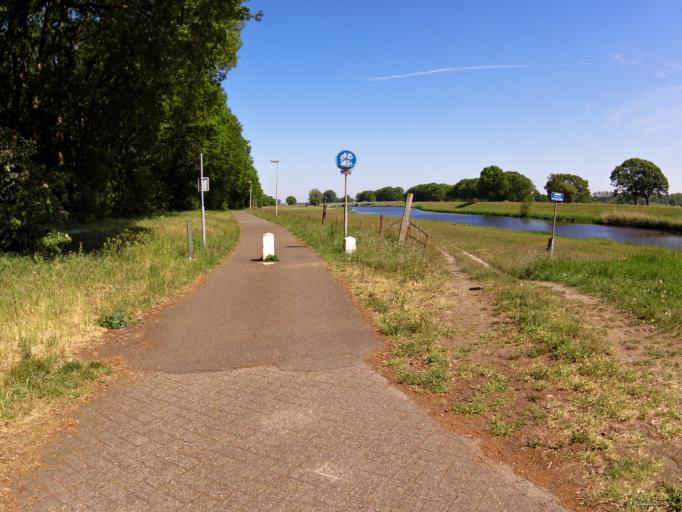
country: NL
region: North Brabant
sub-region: Gemeente Waalwijk
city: Waalwijk
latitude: 51.6839
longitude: 5.1014
